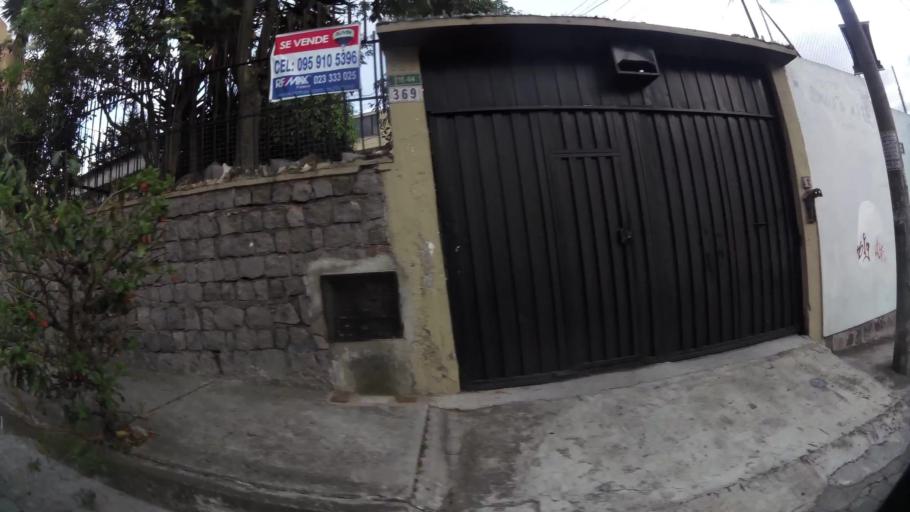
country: EC
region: Pichincha
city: Quito
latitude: -0.1494
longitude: -78.4642
